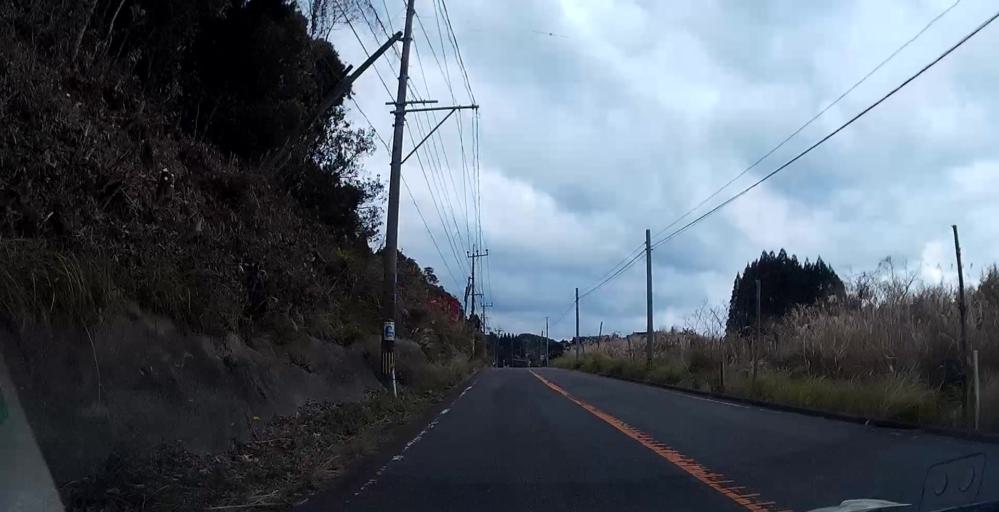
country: JP
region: Kagoshima
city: Akune
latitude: 32.0992
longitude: 130.1765
